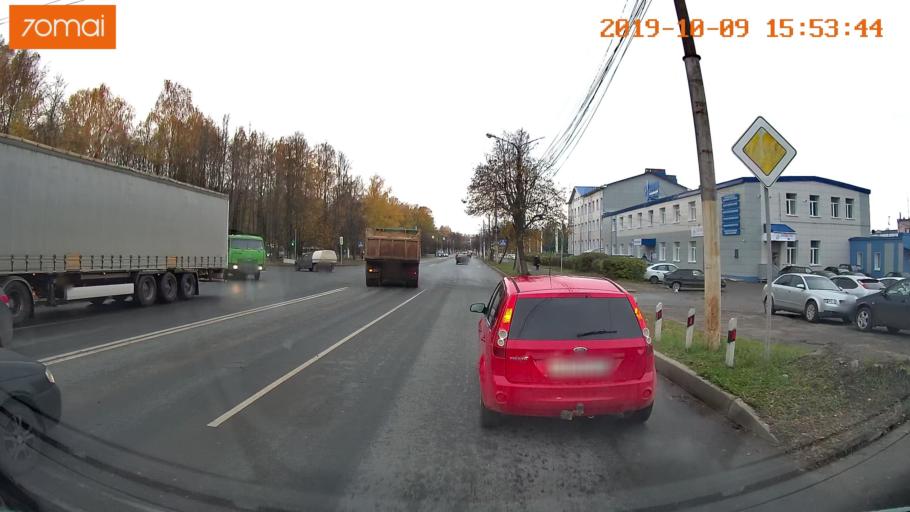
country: RU
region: Kostroma
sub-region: Kostromskoy Rayon
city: Kostroma
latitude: 57.7845
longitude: 40.9606
